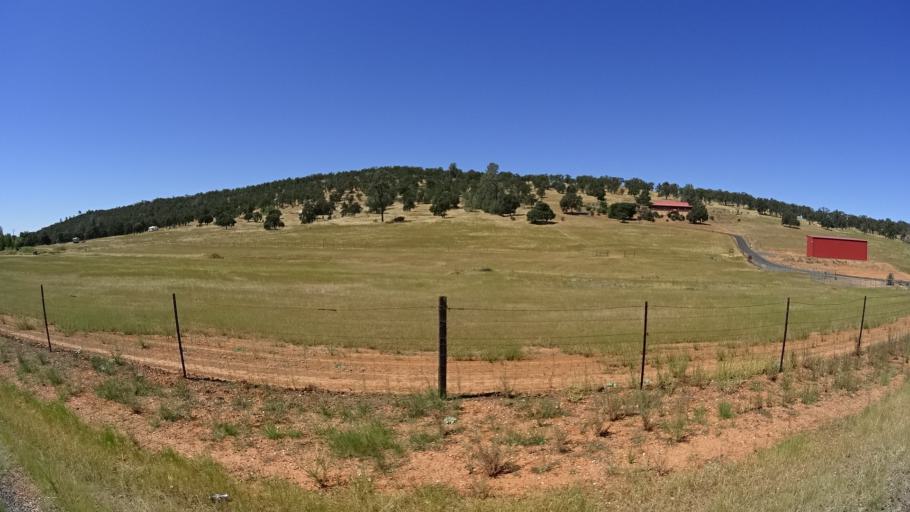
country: US
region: California
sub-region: Calaveras County
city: Copperopolis
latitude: 38.0214
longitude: -120.6831
